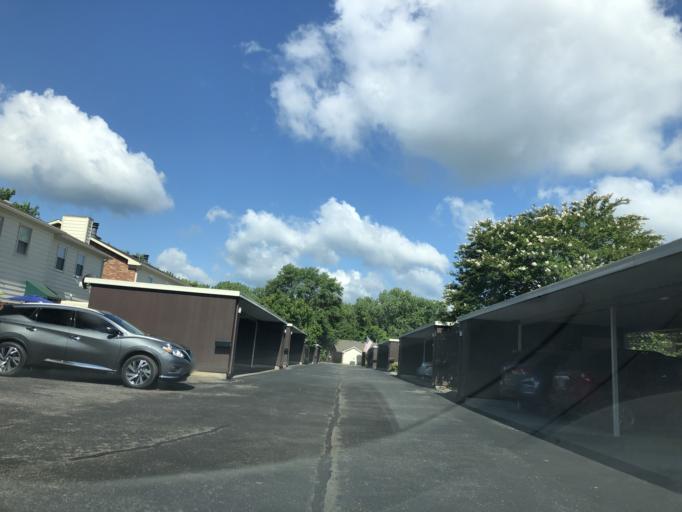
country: US
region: Tennessee
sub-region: Davidson County
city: Belle Meade
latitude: 36.0674
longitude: -86.9512
